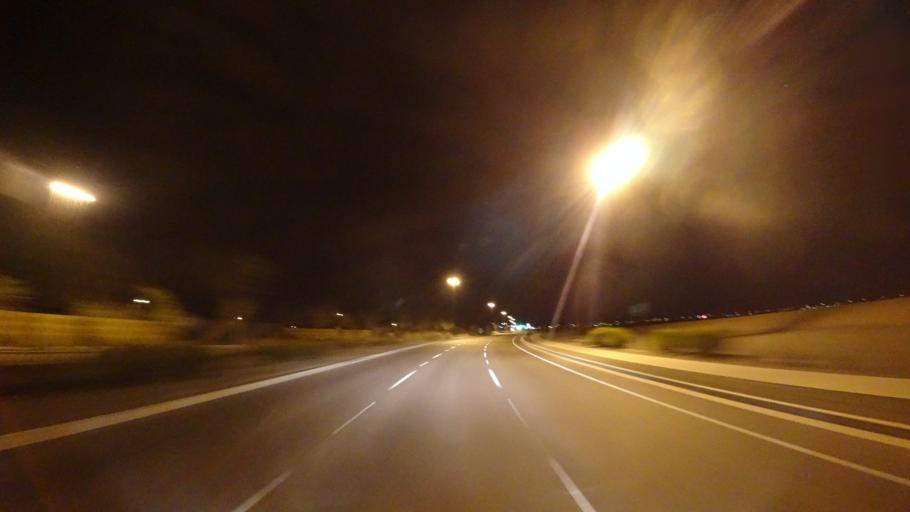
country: US
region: Arizona
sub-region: Maricopa County
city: Queen Creek
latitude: 33.3015
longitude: -111.6869
